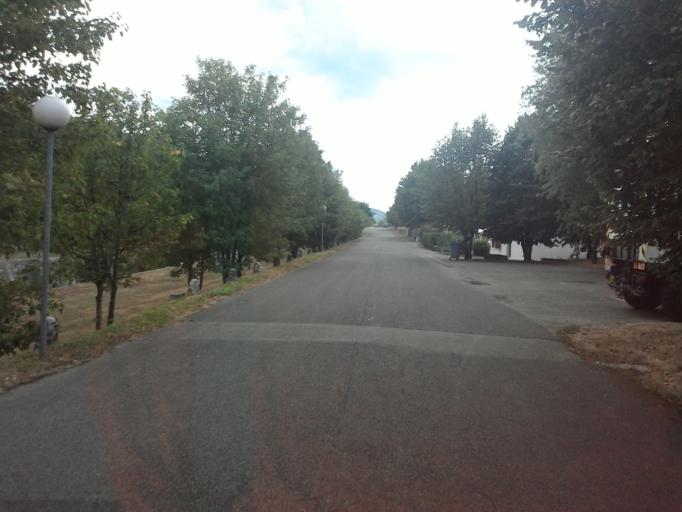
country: FR
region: Rhone-Alpes
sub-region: Departement de l'Ain
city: Sault-Brenaz
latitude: 45.8525
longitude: 5.4080
